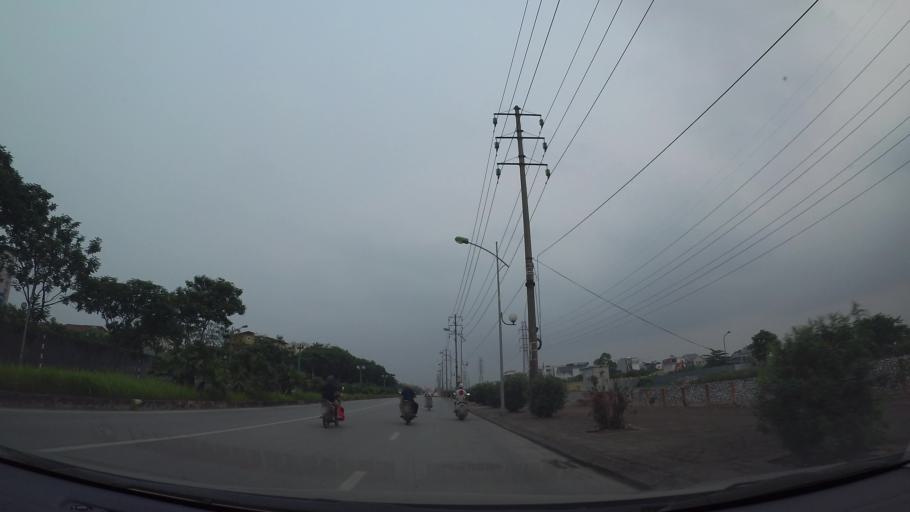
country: VN
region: Ha Noi
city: Trau Quy
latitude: 21.0576
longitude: 105.9040
